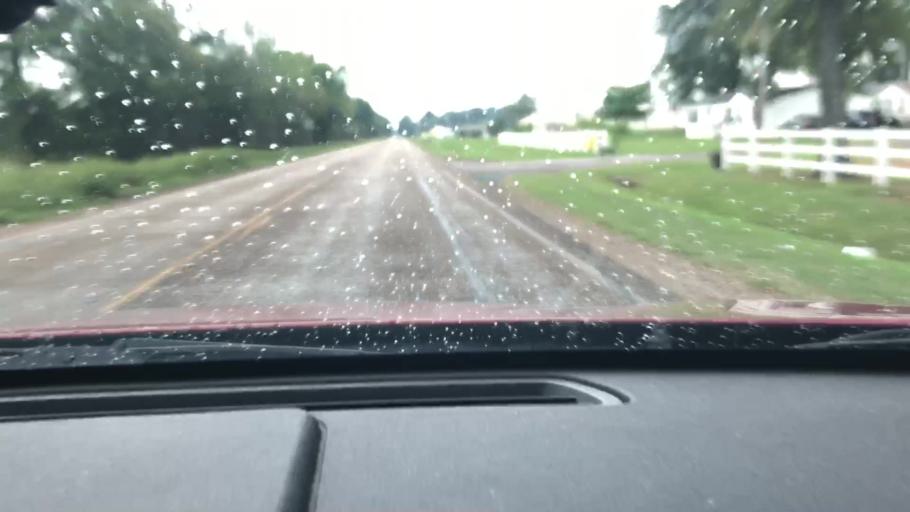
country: US
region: Texas
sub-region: Bowie County
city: Nash
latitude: 33.4420
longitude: -94.1377
